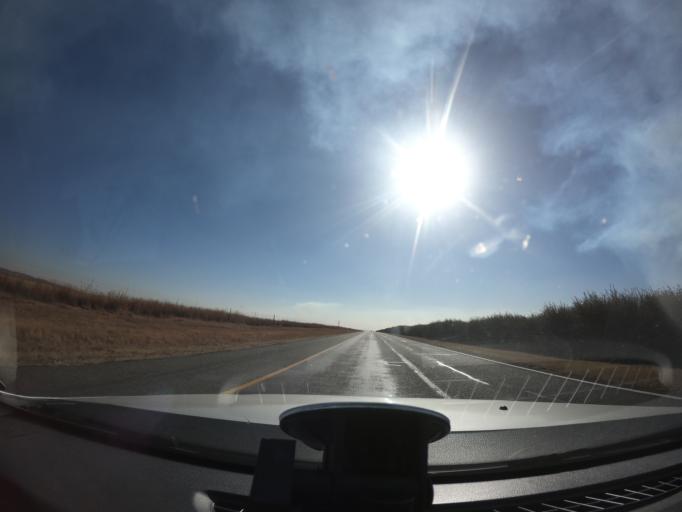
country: ZA
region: Gauteng
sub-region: Sedibeng District Municipality
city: Heidelberg
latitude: -26.4410
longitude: 28.3074
